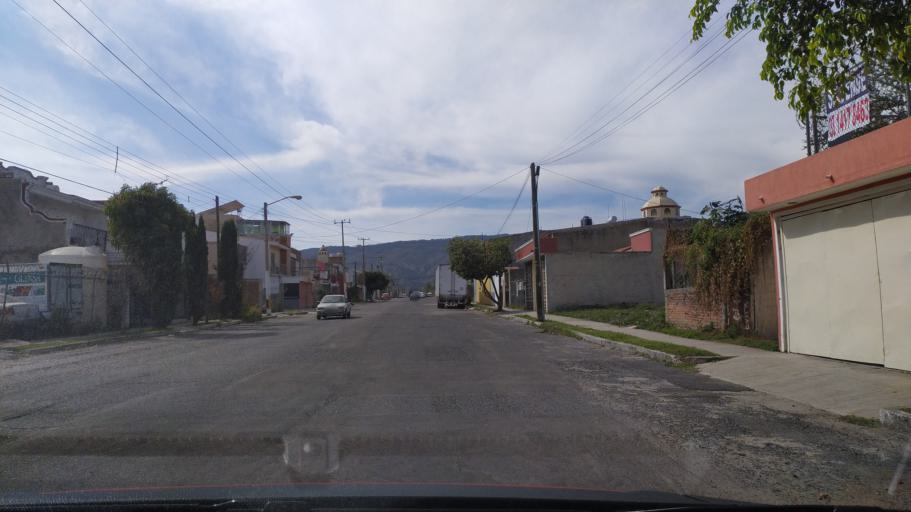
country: MX
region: Jalisco
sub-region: Tlajomulco de Zuniga
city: Palomar
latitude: 20.6281
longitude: -103.4703
